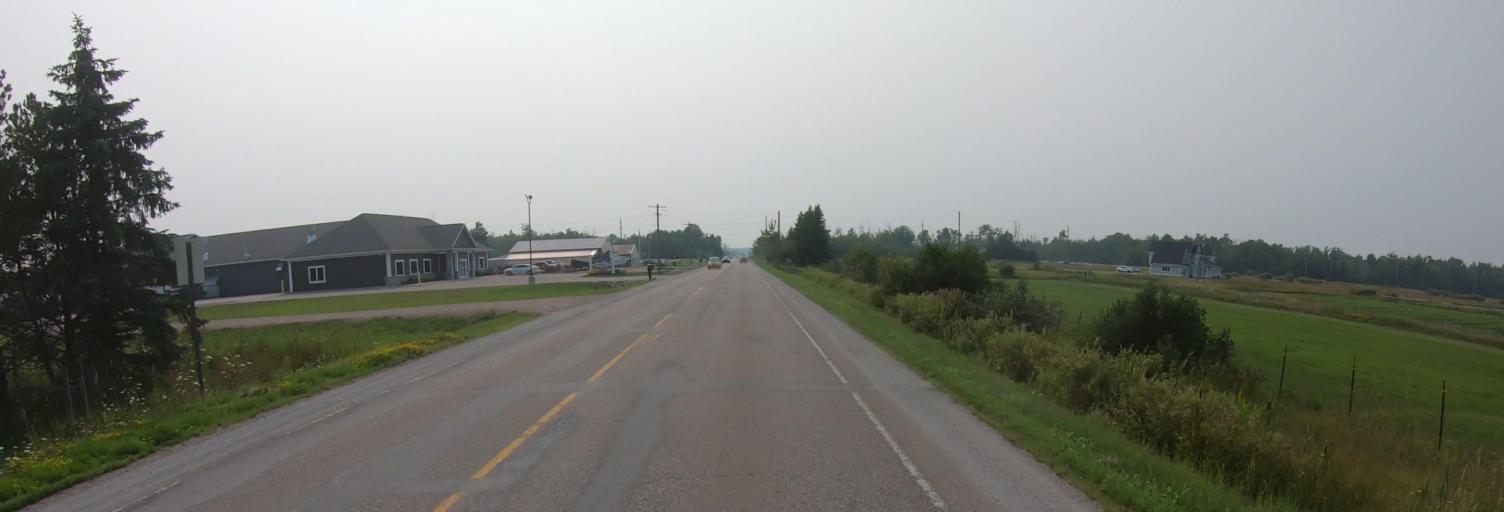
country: US
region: Michigan
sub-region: Chippewa County
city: Sault Ste. Marie
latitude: 46.4632
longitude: -84.3445
